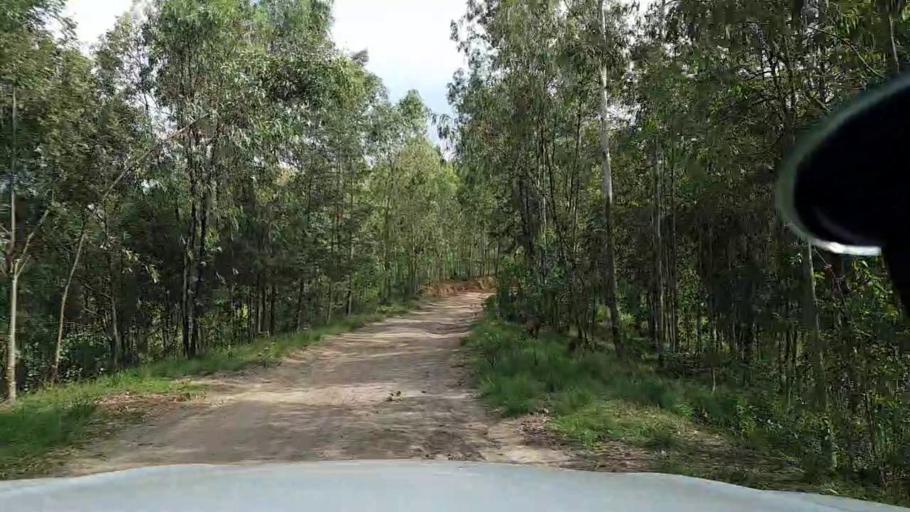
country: RW
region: Kigali
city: Kigali
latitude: -1.7828
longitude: 29.8376
